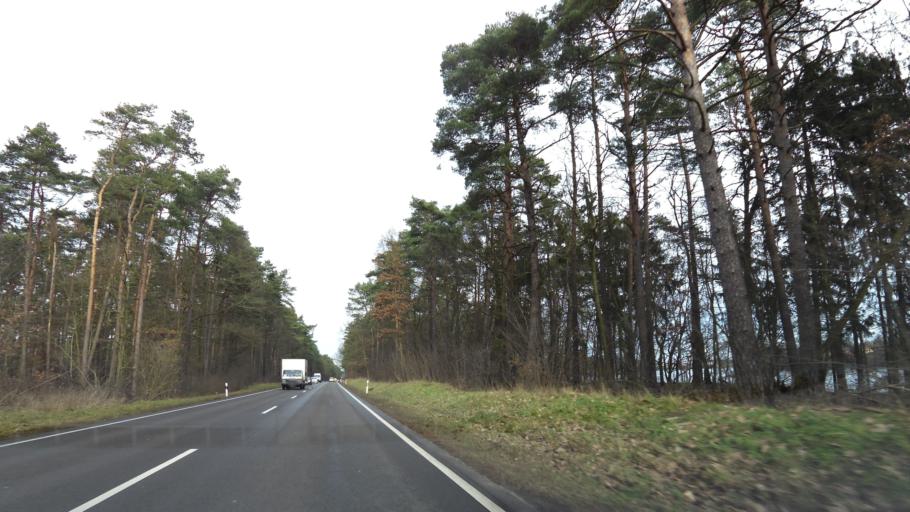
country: DE
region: Brandenburg
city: Strausberg
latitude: 52.5702
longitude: 13.8631
